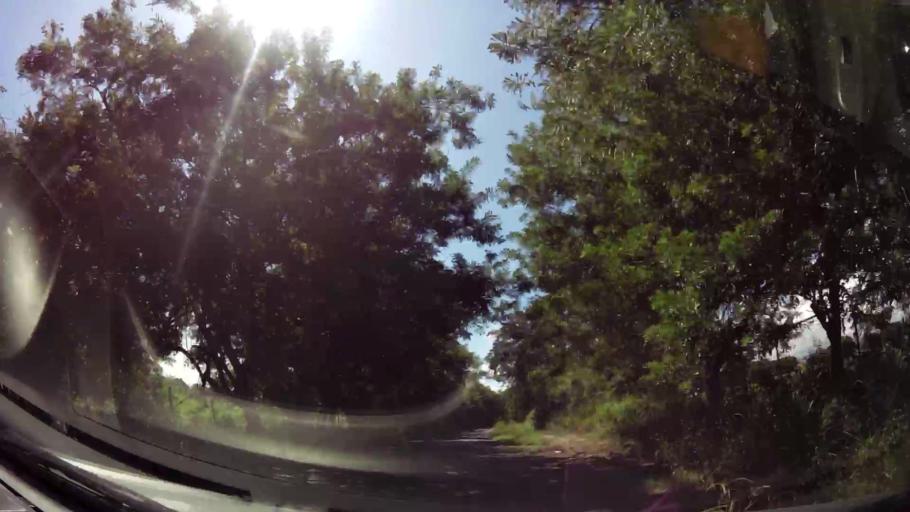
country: PA
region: Panama
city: Nueva Gorgona
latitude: 8.5572
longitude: -79.8582
